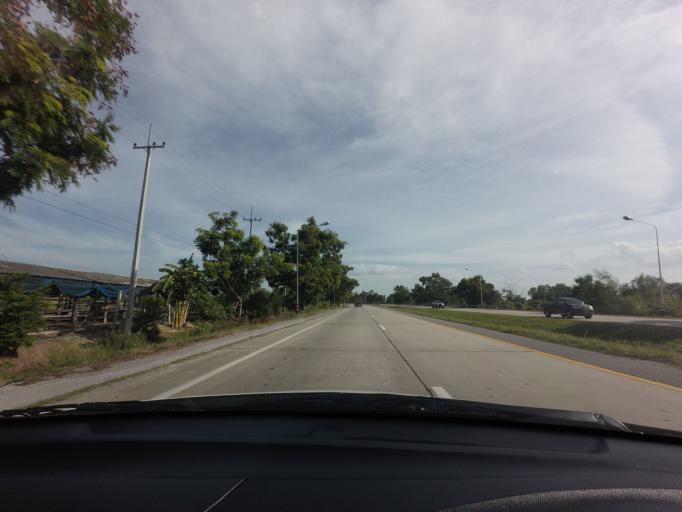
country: TH
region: Suphan Buri
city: Suphan Buri
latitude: 14.4755
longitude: 100.0400
